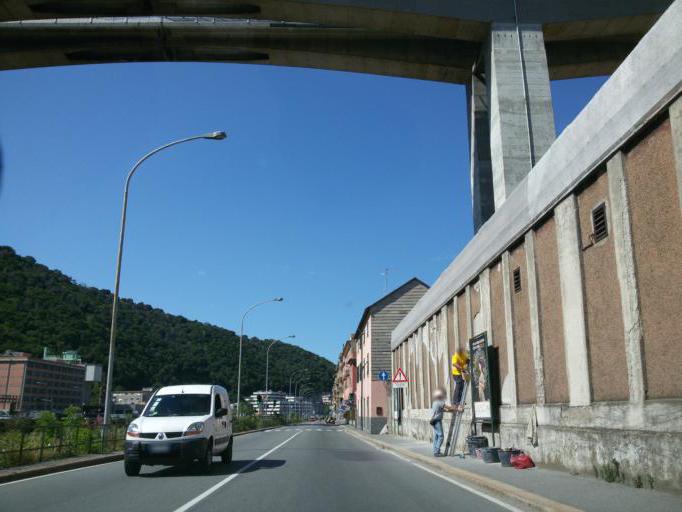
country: IT
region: Liguria
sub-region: Provincia di Genova
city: Genoa
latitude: 44.4339
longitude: 8.9605
